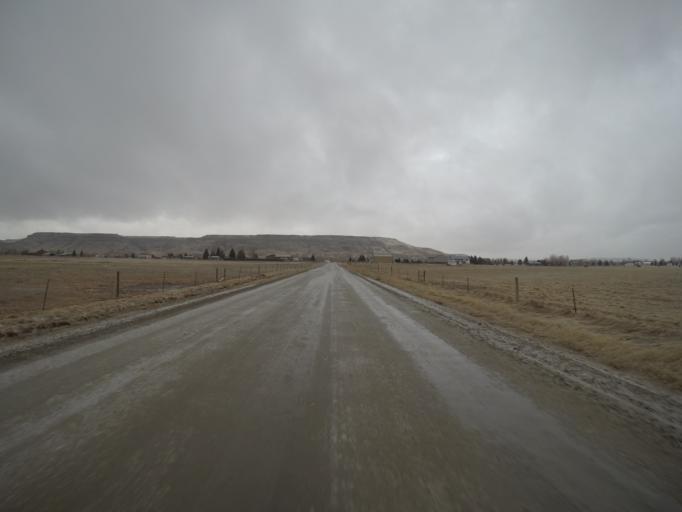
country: US
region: Montana
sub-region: Stillwater County
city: Absarokee
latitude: 45.5262
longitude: -109.4526
